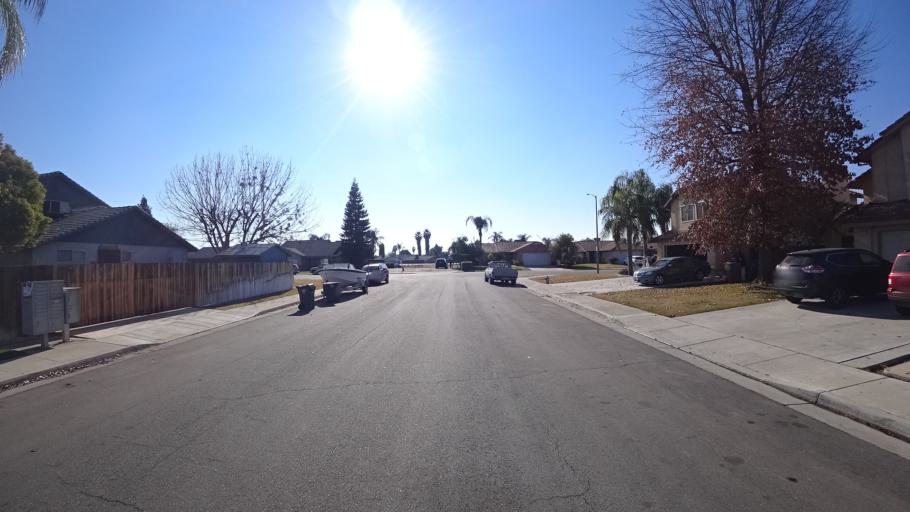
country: US
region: California
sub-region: Kern County
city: Greenfield
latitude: 35.2935
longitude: -119.0523
